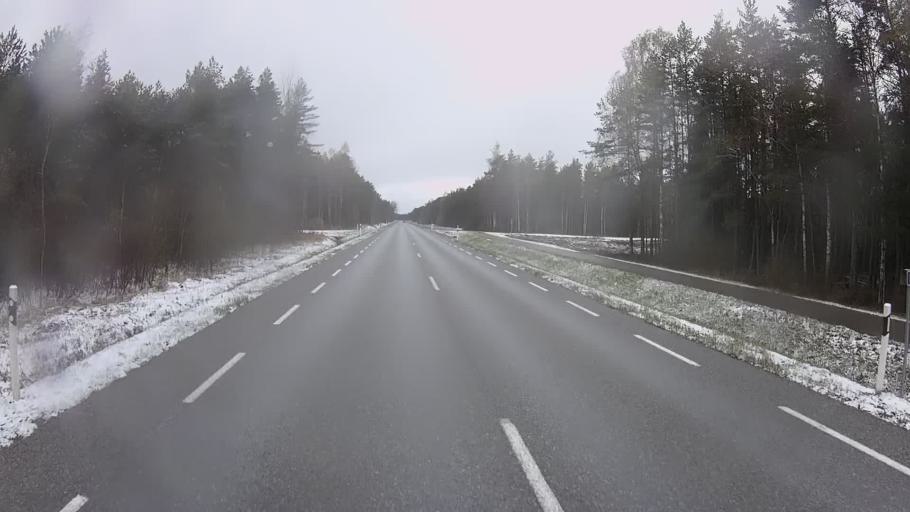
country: EE
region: Hiiumaa
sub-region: Kaerdla linn
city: Kardla
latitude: 59.0105
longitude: 22.6572
